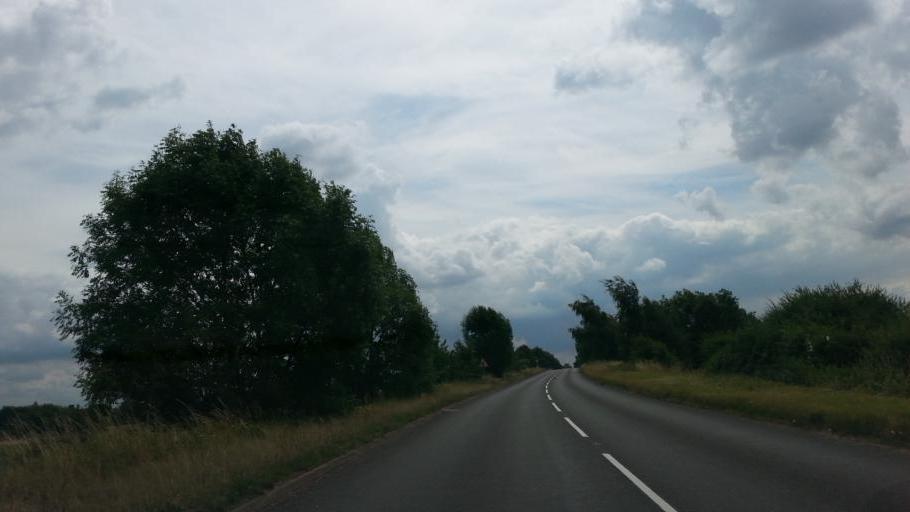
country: GB
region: England
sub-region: Staffordshire
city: Alrewas
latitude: 52.7336
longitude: -1.7611
